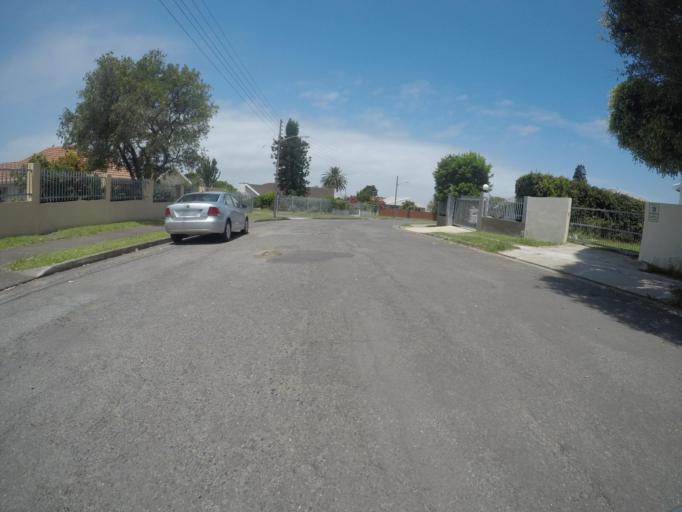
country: ZA
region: Eastern Cape
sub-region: Buffalo City Metropolitan Municipality
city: East London
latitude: -33.0020
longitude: 27.9193
